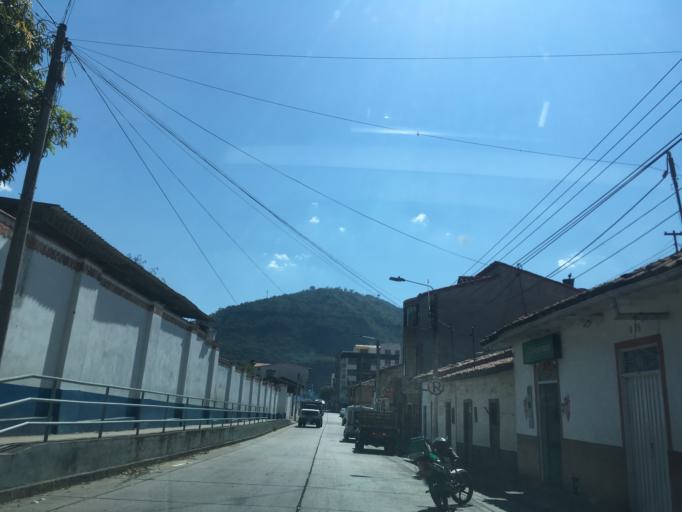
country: CO
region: Santander
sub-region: San Gil
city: San Gil
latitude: 6.5568
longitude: -73.1293
